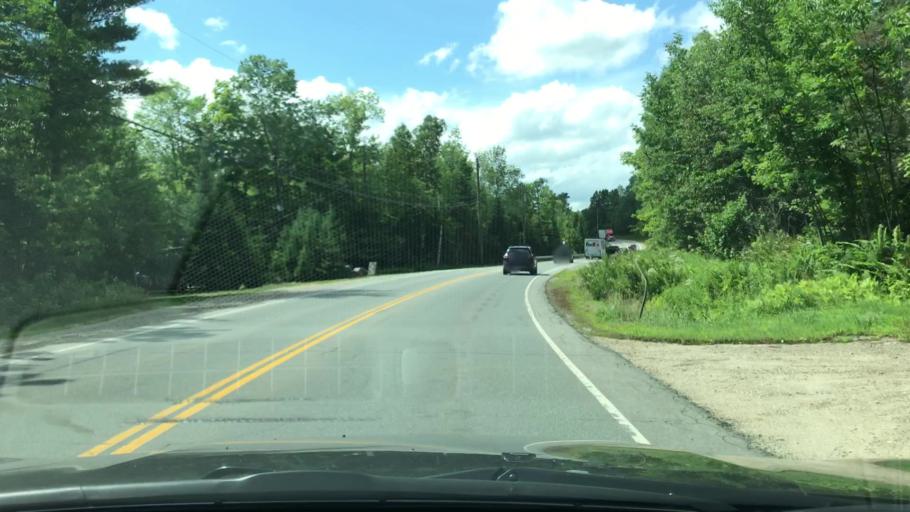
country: US
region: New Hampshire
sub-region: Coos County
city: Jefferson
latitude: 44.3636
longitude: -71.3903
